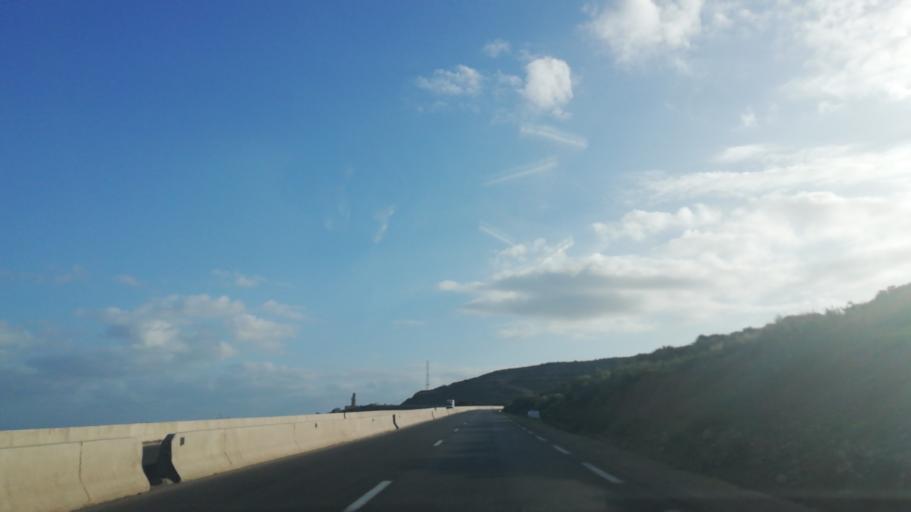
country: DZ
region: Mostaganem
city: Mostaganem
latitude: 36.1075
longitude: 0.2199
